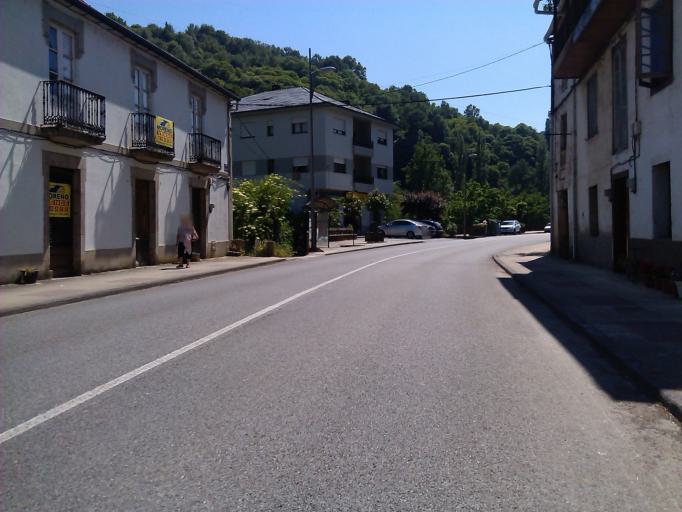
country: ES
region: Galicia
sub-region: Provincia de Lugo
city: Samos
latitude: 42.7297
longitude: -7.3272
